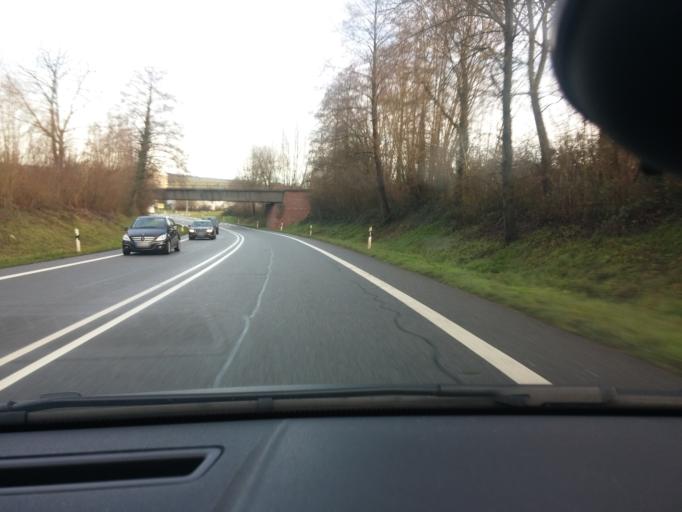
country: DE
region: Hesse
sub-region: Regierungsbezirk Darmstadt
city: Bad Konig
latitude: 49.7464
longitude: 9.0008
